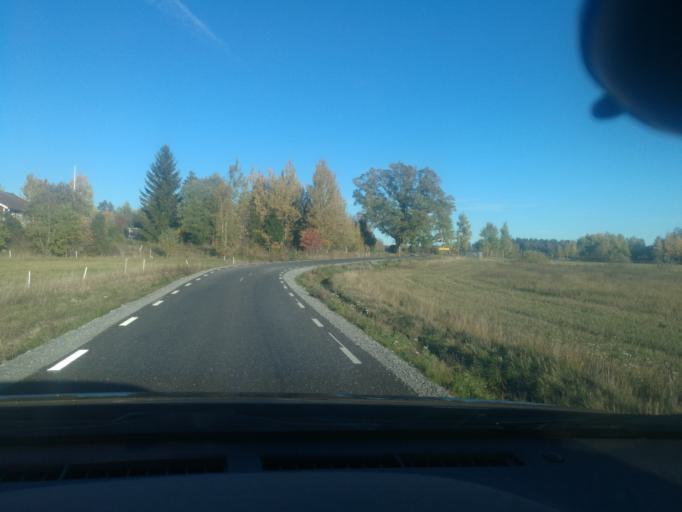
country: SE
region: Vaestmanland
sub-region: Kopings Kommun
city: Koping
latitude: 59.5670
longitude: 16.0646
